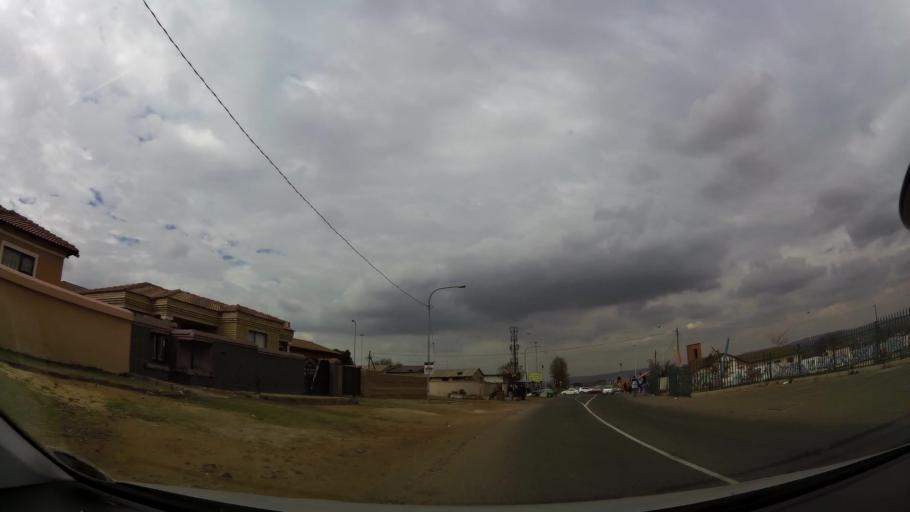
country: ZA
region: Gauteng
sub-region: City of Johannesburg Metropolitan Municipality
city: Soweto
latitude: -26.2806
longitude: 27.8586
